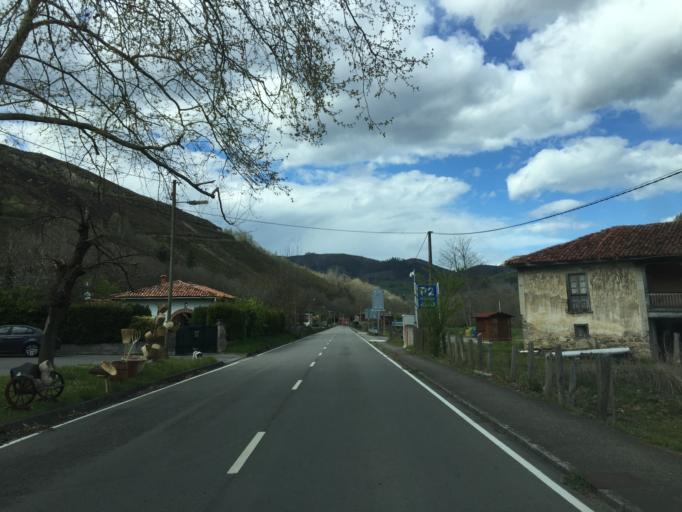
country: ES
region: Asturias
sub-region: Province of Asturias
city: Cangas de Onis
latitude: 43.3362
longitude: -5.0838
